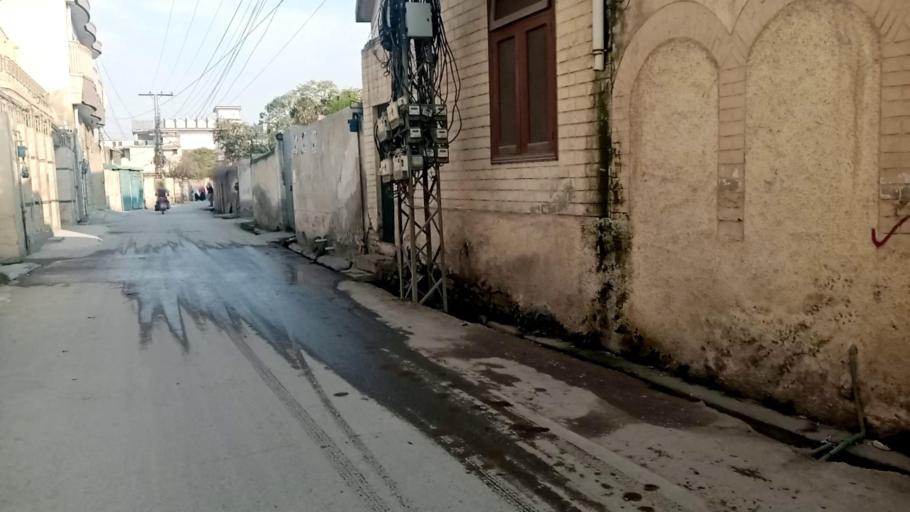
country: PK
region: Khyber Pakhtunkhwa
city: Peshawar
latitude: 34.0028
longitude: 71.4714
